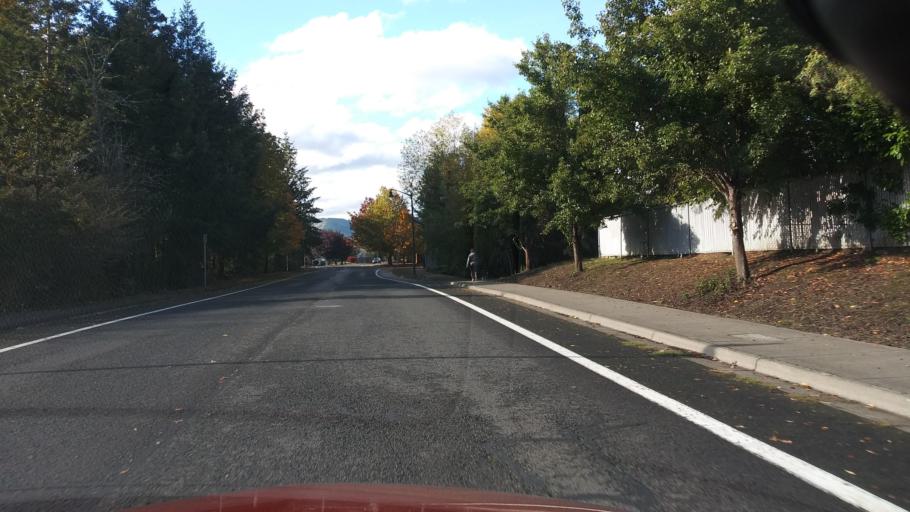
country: US
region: Oregon
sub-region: Washington County
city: Forest Grove
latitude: 45.5337
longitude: -123.1145
